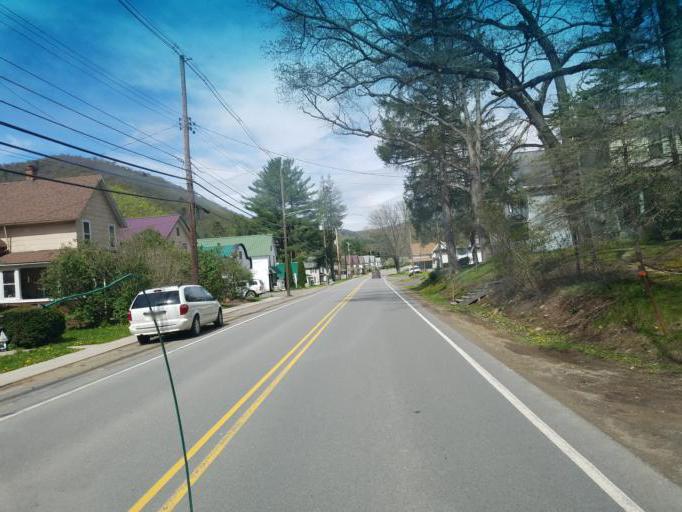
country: US
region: Pennsylvania
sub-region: Potter County
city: Galeton
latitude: 41.7377
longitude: -77.6528
